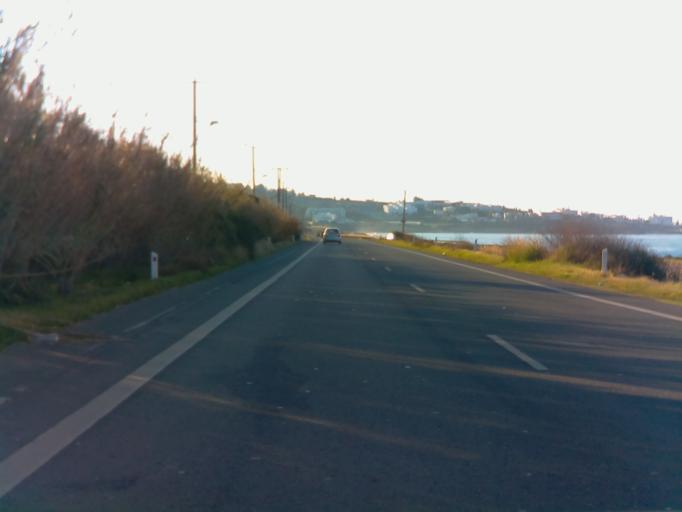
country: CY
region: Pafos
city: Kissonerga
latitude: 34.8427
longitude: 32.3876
